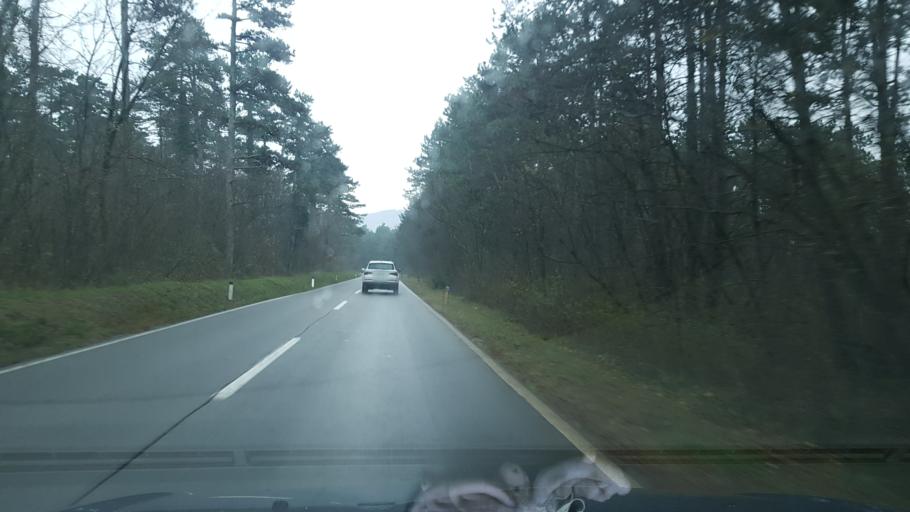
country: SI
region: Sezana
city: Sezana
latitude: 45.7318
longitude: 13.8673
